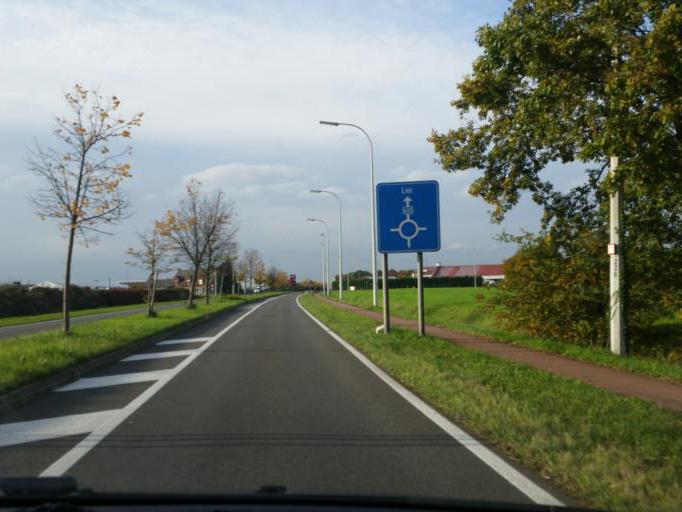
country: BE
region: Flanders
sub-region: Provincie Antwerpen
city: Putte
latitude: 51.0925
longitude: 4.6257
